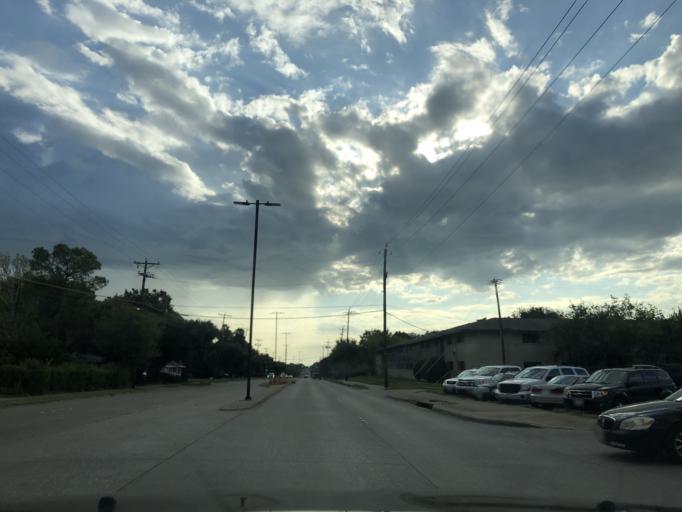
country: US
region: Texas
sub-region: Dallas County
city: Garland
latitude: 32.8787
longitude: -96.6462
